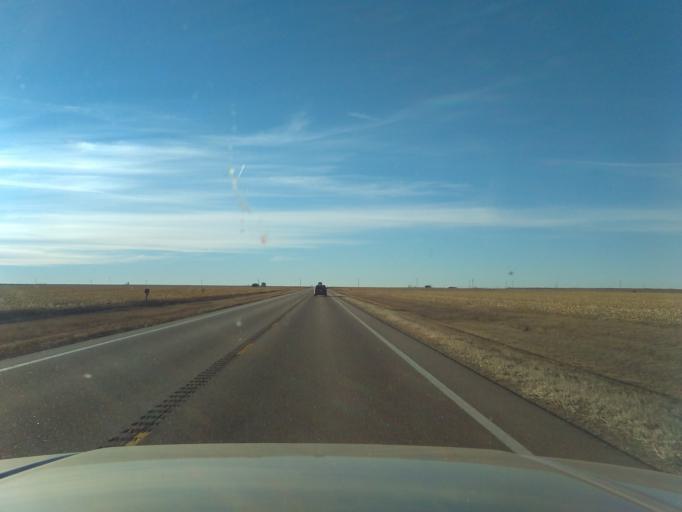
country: US
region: Kansas
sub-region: Thomas County
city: Colby
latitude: 39.4649
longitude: -100.7480
